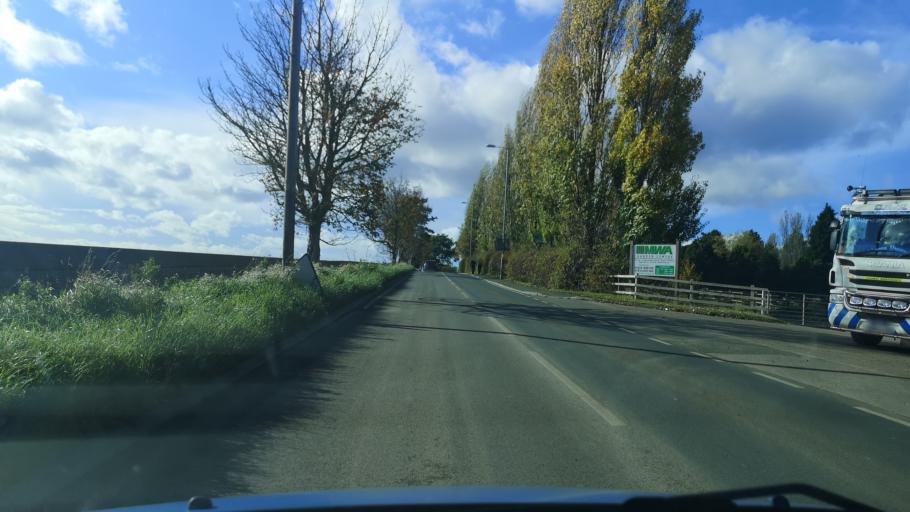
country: GB
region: England
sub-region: City and Borough of Wakefield
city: Normanton
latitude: 53.7060
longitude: -1.4487
